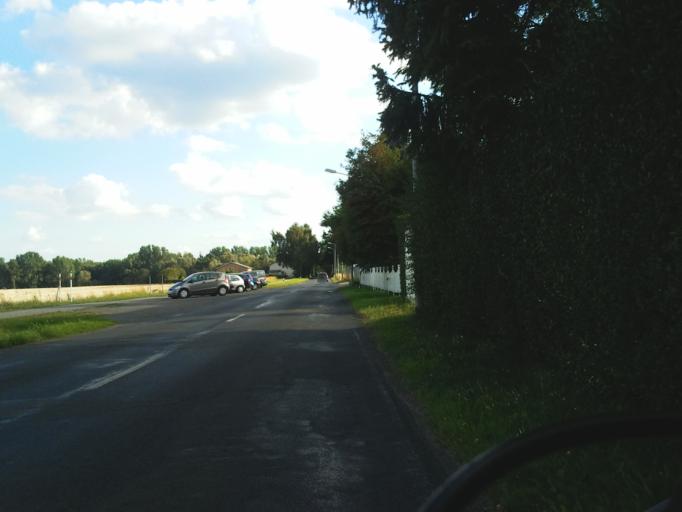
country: DE
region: Mecklenburg-Vorpommern
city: Dierkow-West
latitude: 54.1270
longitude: 12.1053
